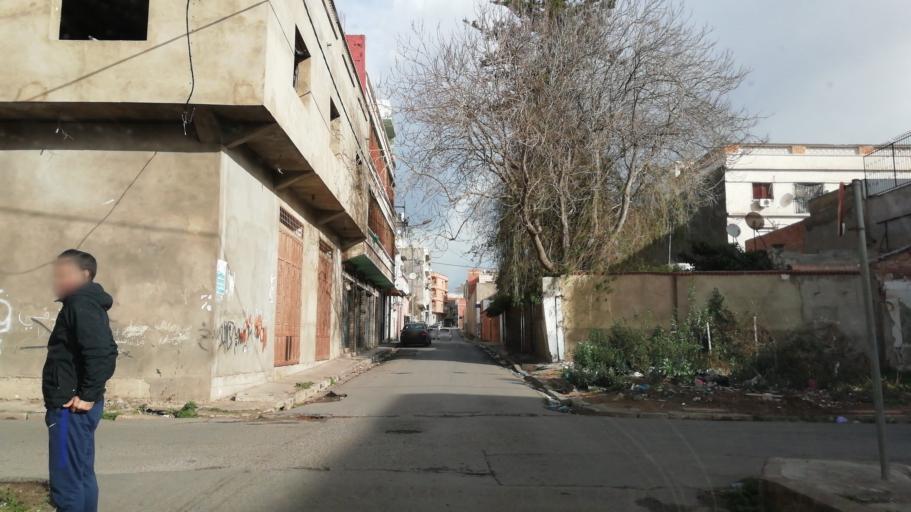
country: DZ
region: Oran
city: Oran
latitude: 35.6971
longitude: -0.6214
